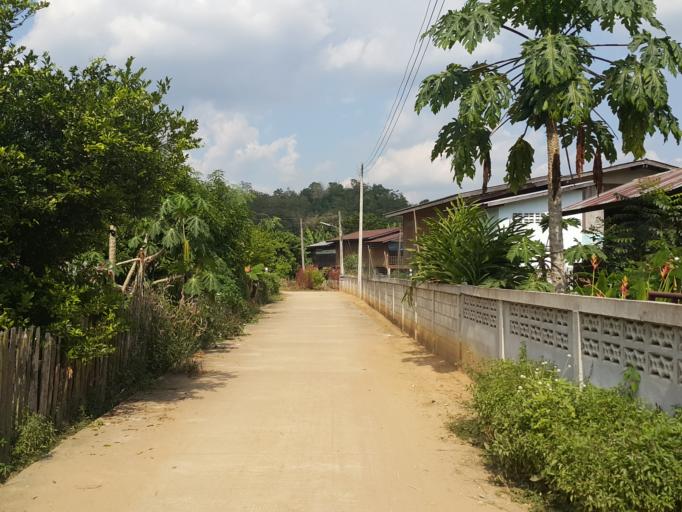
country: TH
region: Sukhothai
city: Thung Saliam
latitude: 17.3298
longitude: 99.4585
